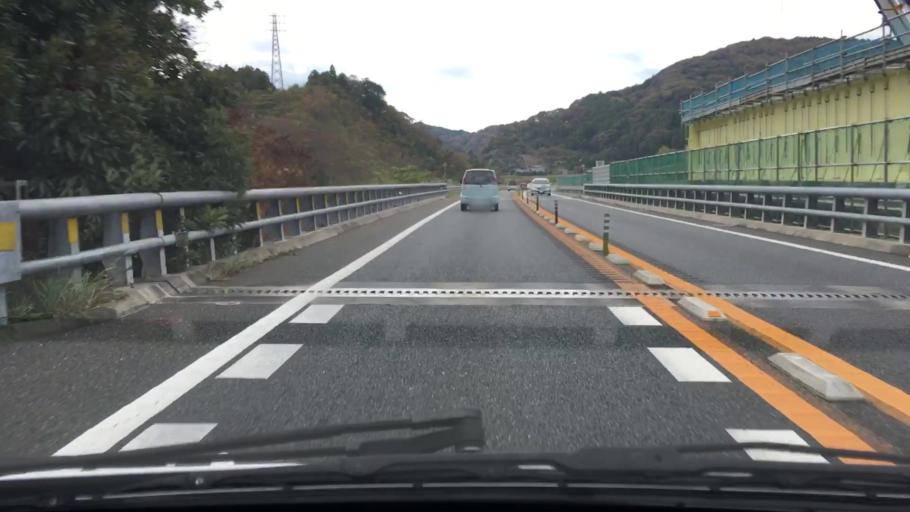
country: JP
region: Chiba
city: Futtsu
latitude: 35.2101
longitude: 139.8834
